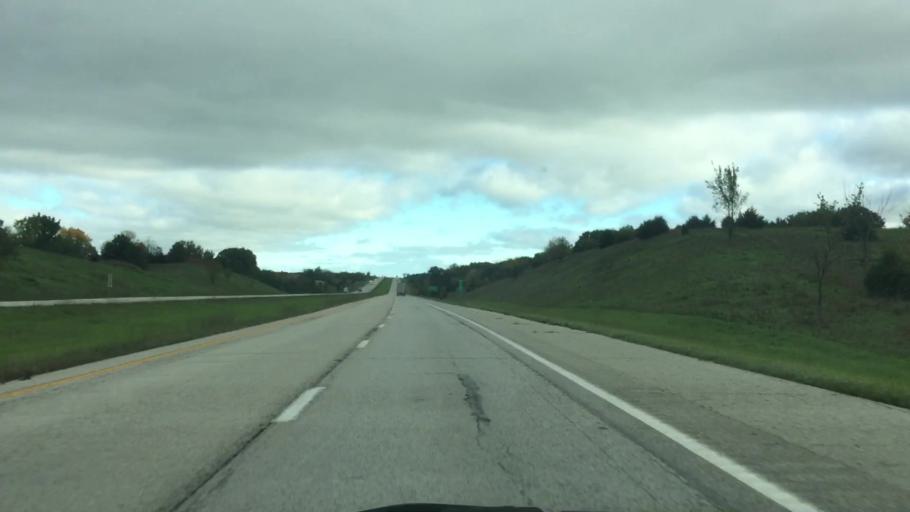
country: US
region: Missouri
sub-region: Harrison County
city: Bethany
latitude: 40.1829
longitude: -94.0146
